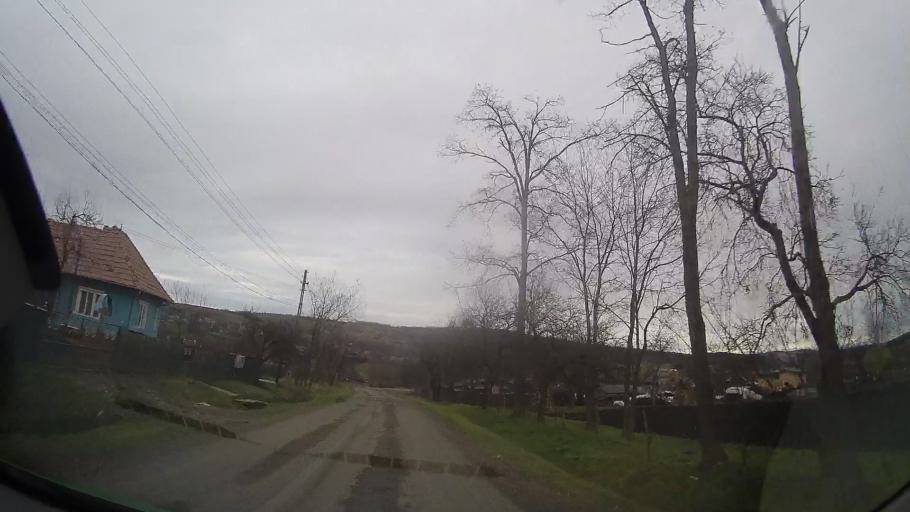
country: RO
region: Mures
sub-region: Comuna Bala
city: Bala
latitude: 46.7054
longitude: 24.4963
